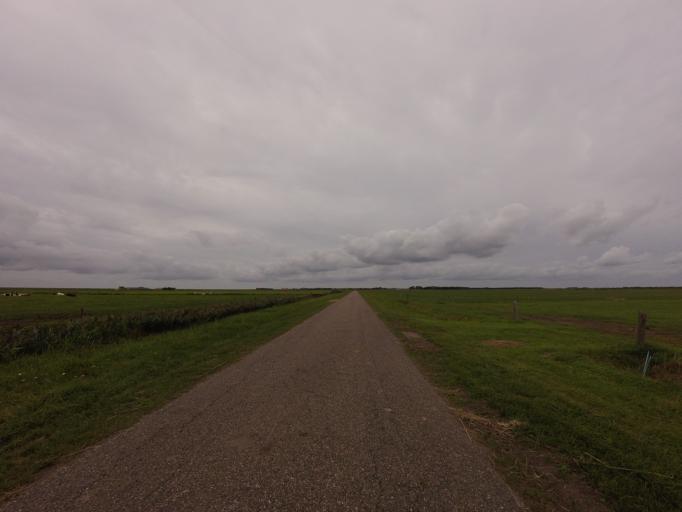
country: NL
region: Friesland
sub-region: Gemeente Ameland
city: Hollum
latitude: 53.4321
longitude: 5.6870
